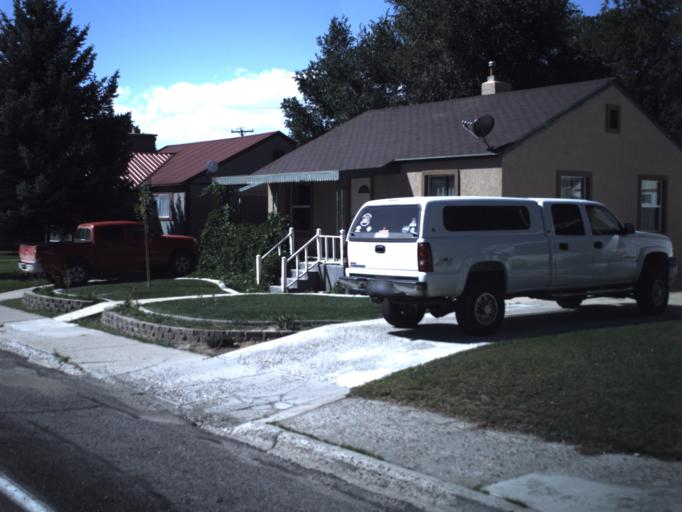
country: US
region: Utah
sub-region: Beaver County
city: Milford
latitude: 38.4009
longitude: -113.0100
